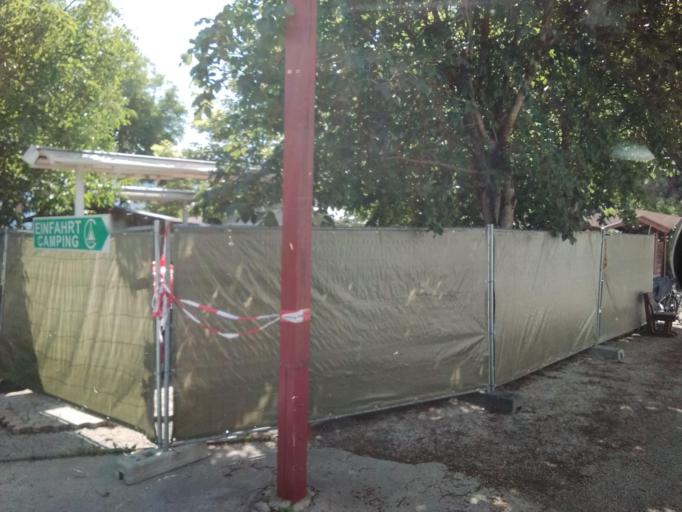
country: AT
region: Tyrol
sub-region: Politischer Bezirk Lienz
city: Amlach
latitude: 46.8136
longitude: 12.7631
